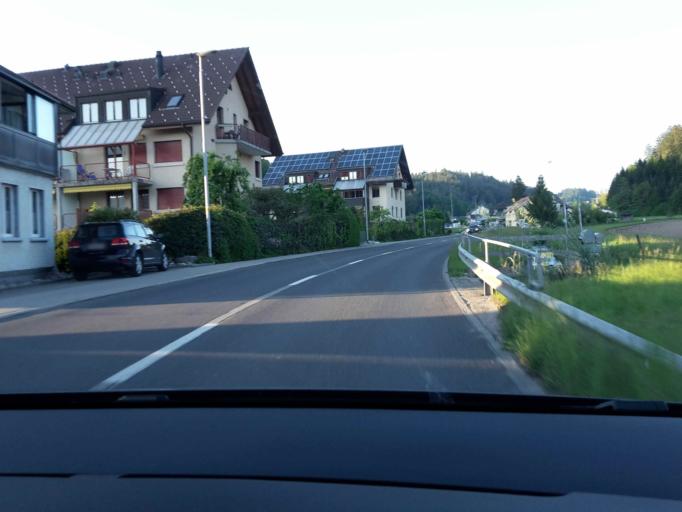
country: CH
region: Bern
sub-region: Emmental District
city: Lutzelfluh
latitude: 47.0198
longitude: 7.6637
